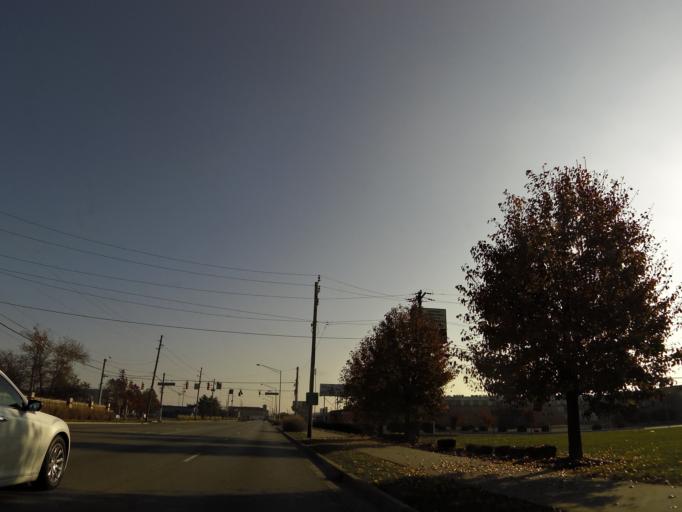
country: US
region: Indiana
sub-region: Marion County
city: Indianapolis
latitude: 39.7892
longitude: -86.1921
